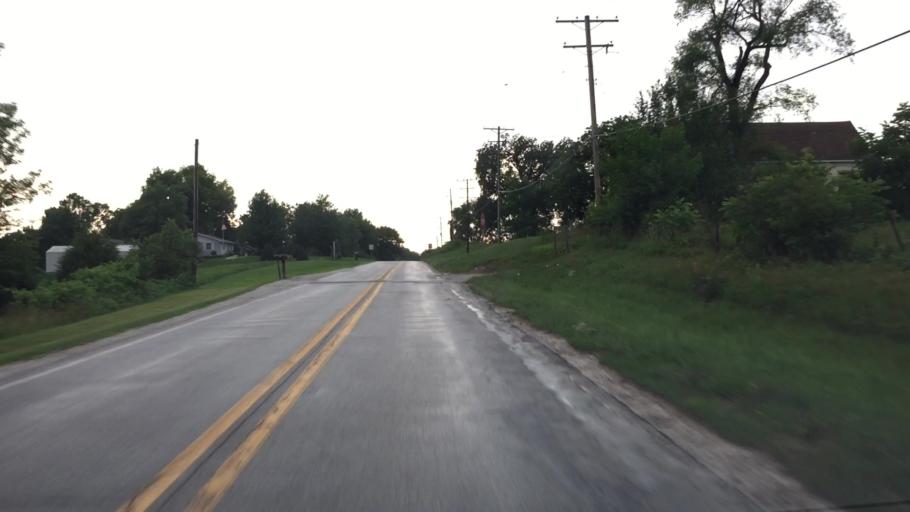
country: US
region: Illinois
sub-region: Hancock County
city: Warsaw
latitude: 40.3565
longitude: -91.4190
